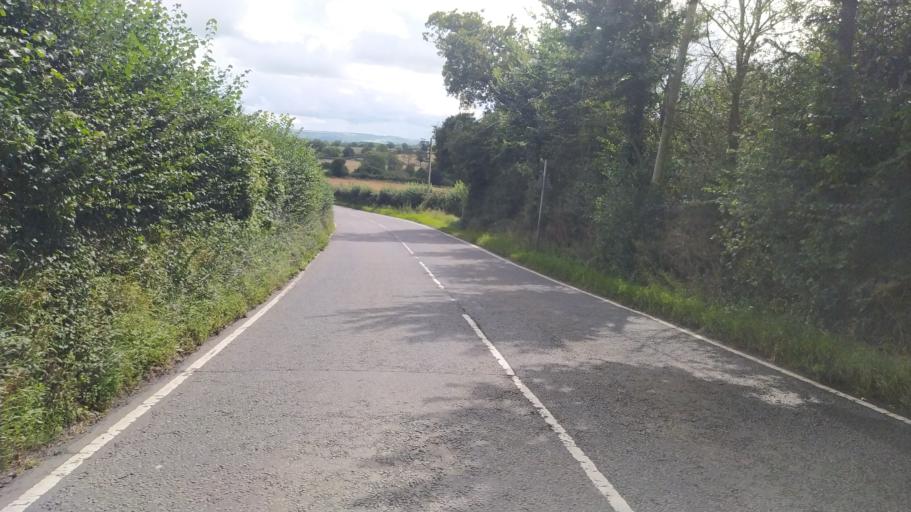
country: GB
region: England
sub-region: Somerset
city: Milborne Port
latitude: 50.9149
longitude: -2.4260
